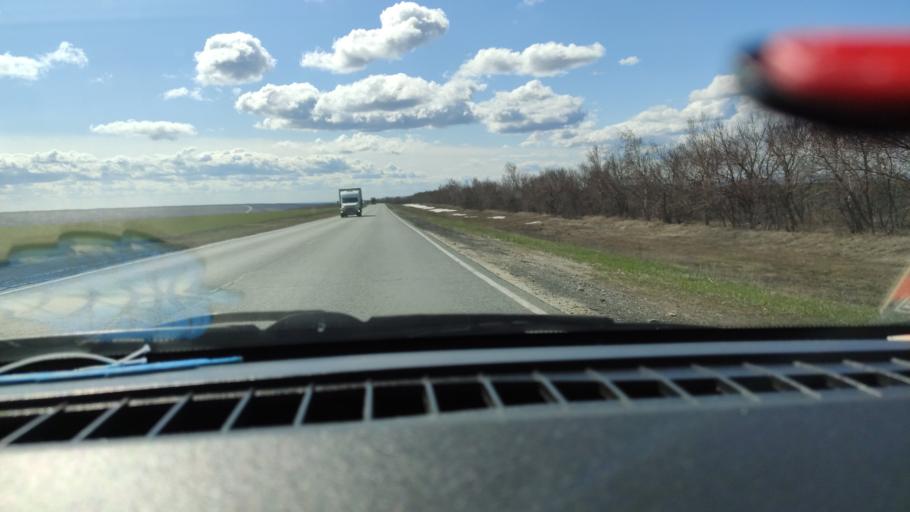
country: RU
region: Saratov
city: Dukhovnitskoye
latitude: 52.7666
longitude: 48.2376
